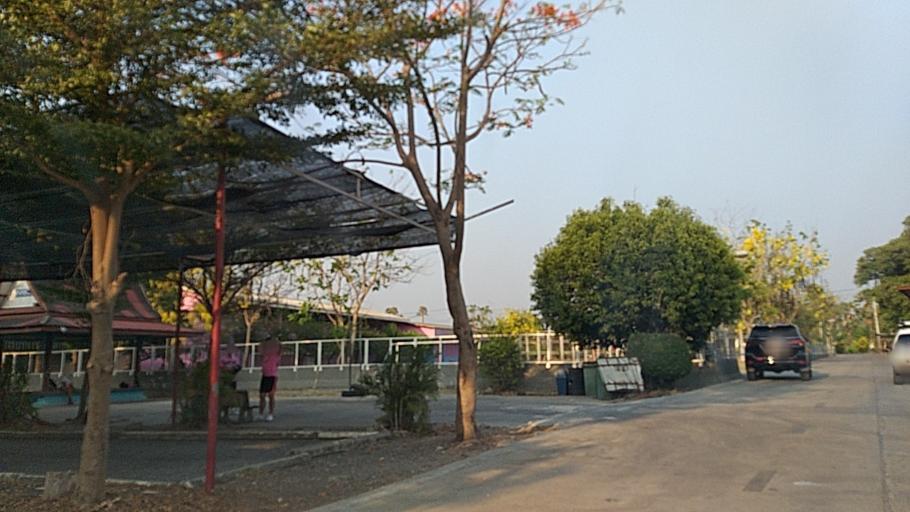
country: TH
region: Phra Nakhon Si Ayutthaya
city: Ban Bang Kadi Pathum Thani
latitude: 14.0044
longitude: 100.5415
